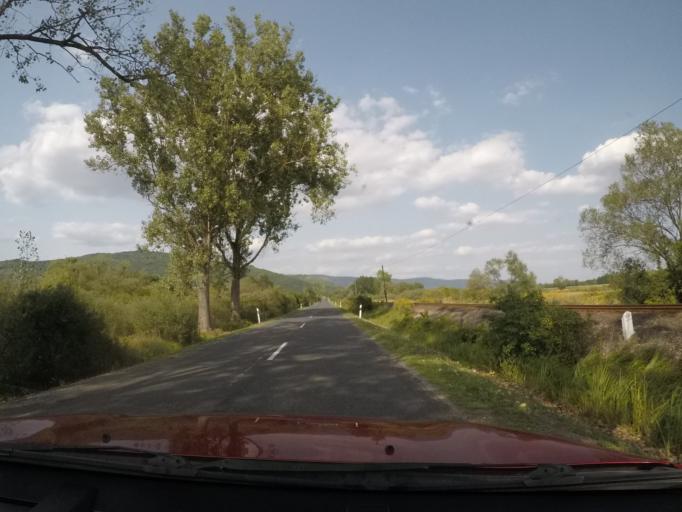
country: HU
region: Borsod-Abauj-Zemplen
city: Szendro
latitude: 48.5093
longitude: 20.7038
